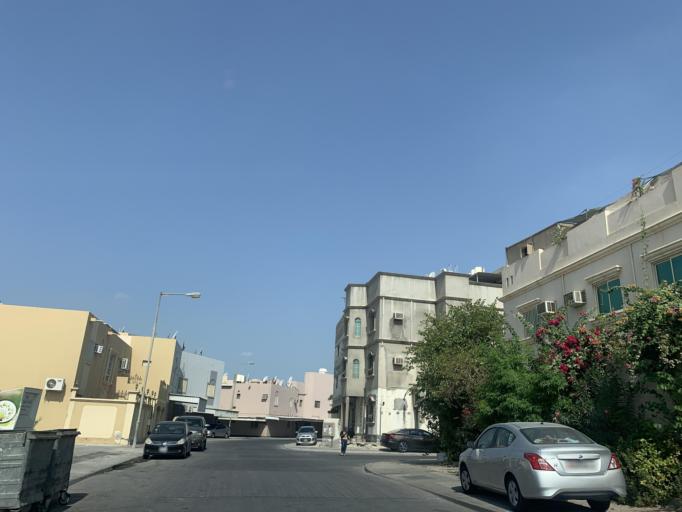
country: BH
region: Central Governorate
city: Madinat Hamad
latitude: 26.1280
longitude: 50.4997
